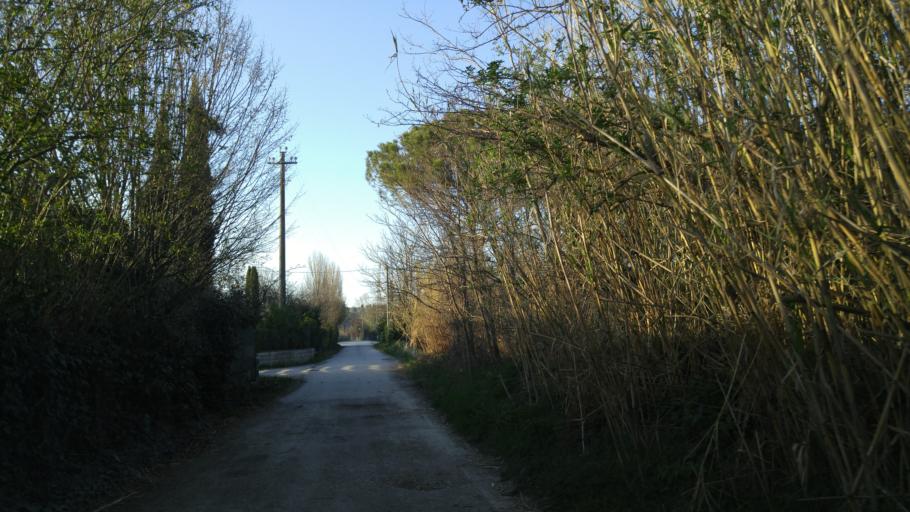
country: IT
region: The Marches
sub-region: Provincia di Pesaro e Urbino
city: Villa Ceccolini
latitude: 43.8942
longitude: 12.8457
